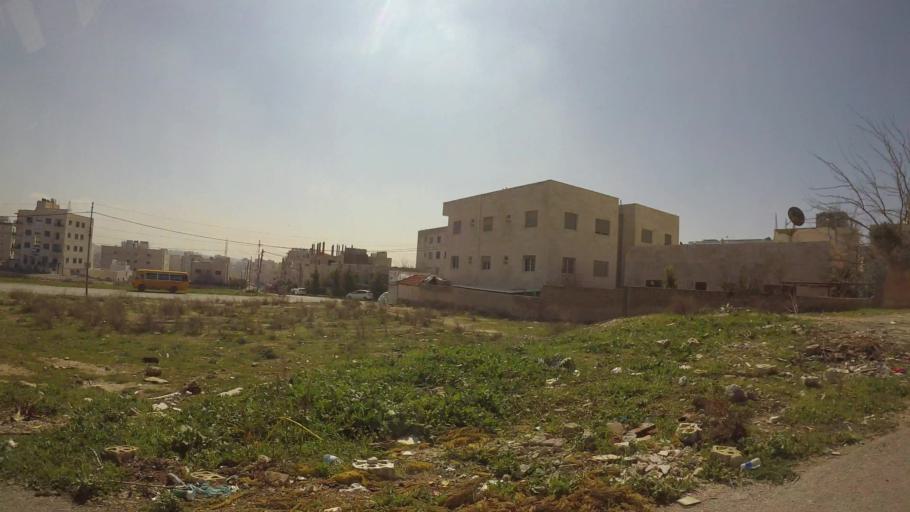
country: JO
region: Amman
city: Al Bunayyat ash Shamaliyah
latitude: 31.8925
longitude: 35.8963
